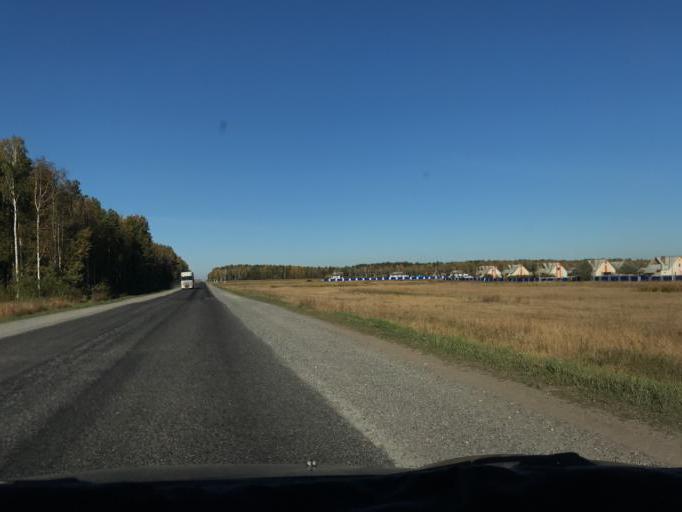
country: BY
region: Gomel
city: Yel'sk
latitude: 51.7934
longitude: 29.1991
